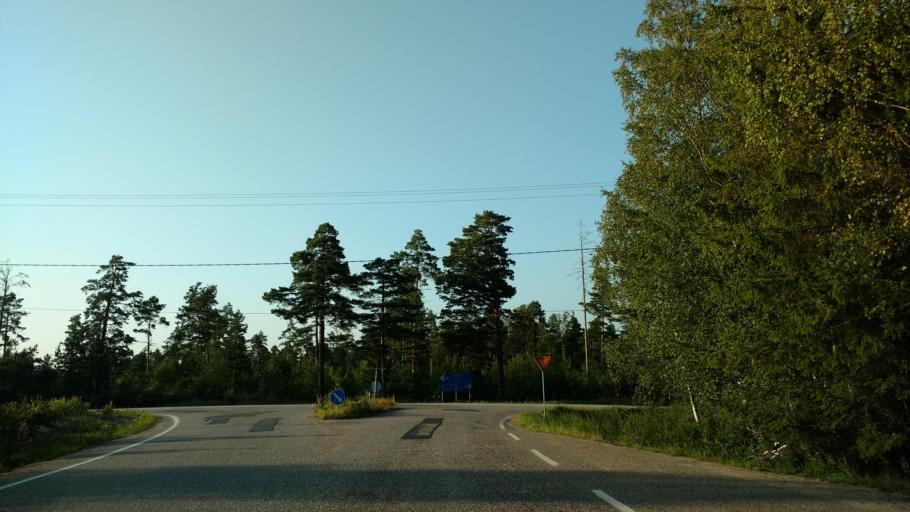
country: FI
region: Varsinais-Suomi
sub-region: Aboland-Turunmaa
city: Dragsfjaerd
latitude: 60.0277
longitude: 22.4612
